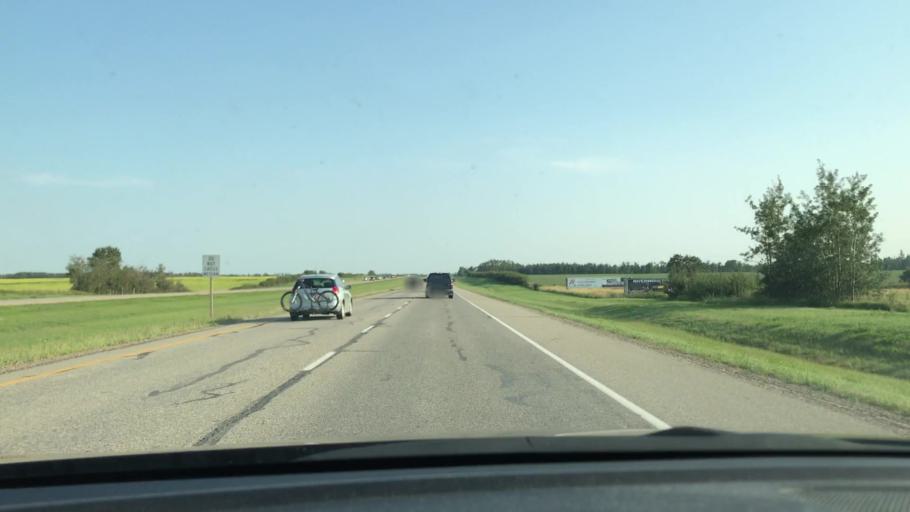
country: CA
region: Alberta
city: Millet
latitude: 53.0779
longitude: -113.5983
